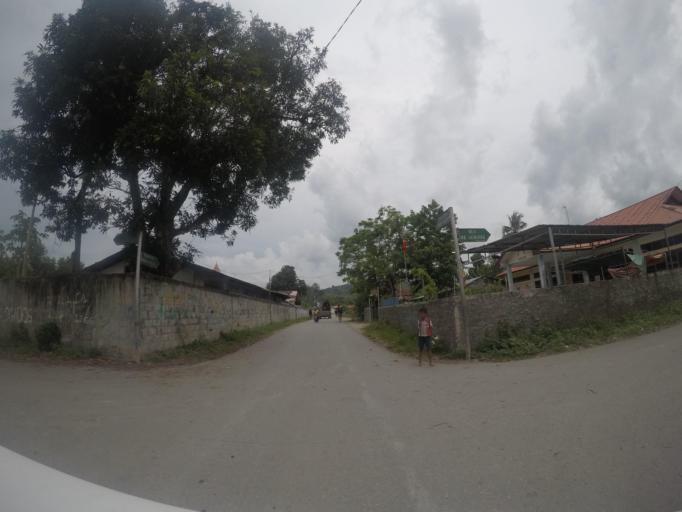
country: TL
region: Viqueque
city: Viqueque
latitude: -8.8702
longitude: 126.3645
